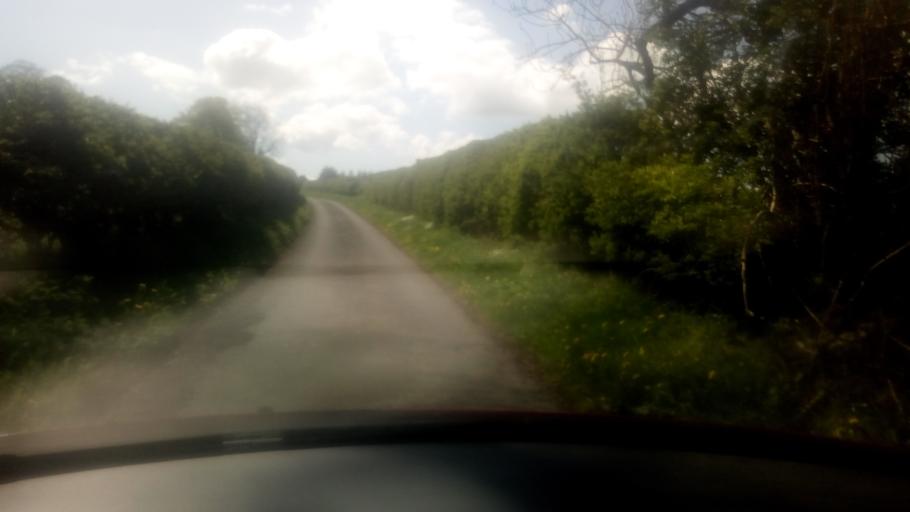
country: GB
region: Scotland
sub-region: The Scottish Borders
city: Hawick
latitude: 55.4212
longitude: -2.7161
